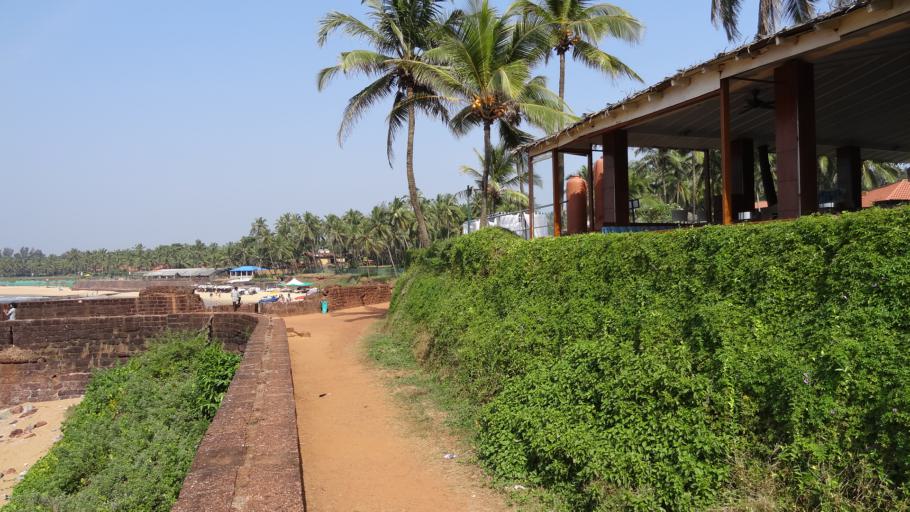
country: IN
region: Goa
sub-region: North Goa
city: Candolim
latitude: 15.4979
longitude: 73.7665
